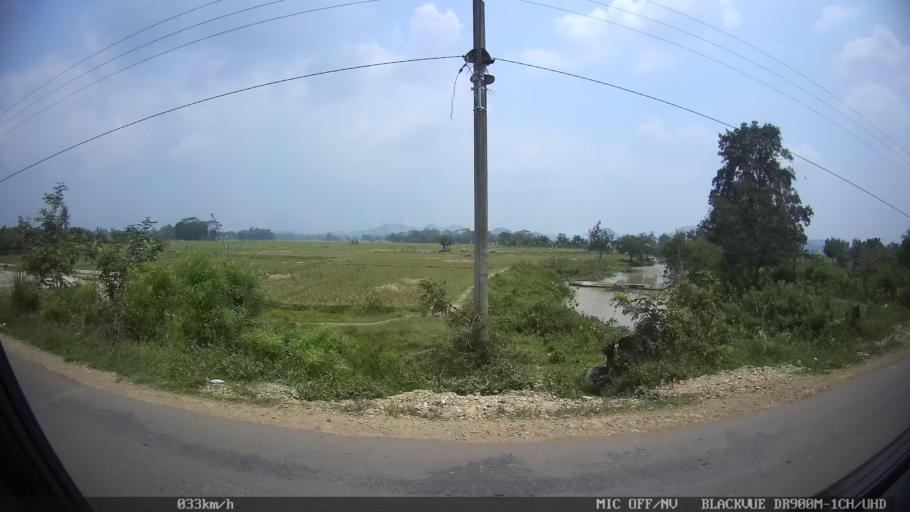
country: ID
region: Lampung
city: Pringsewu
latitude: -5.3534
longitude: 105.0148
